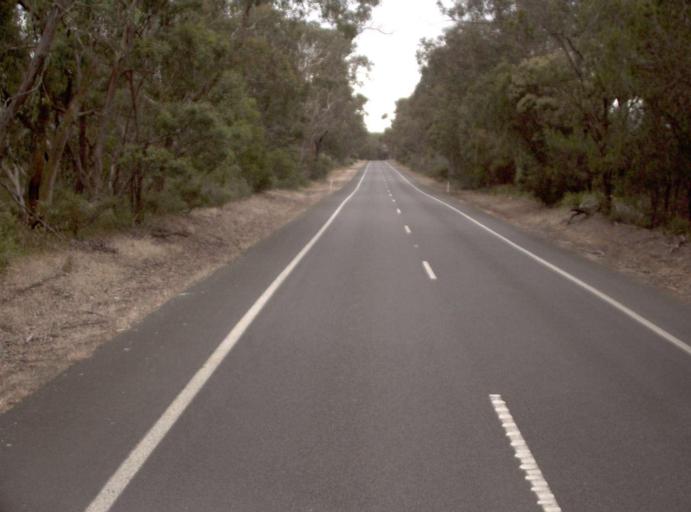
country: AU
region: Victoria
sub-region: Wellington
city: Sale
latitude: -38.2522
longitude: 147.0494
